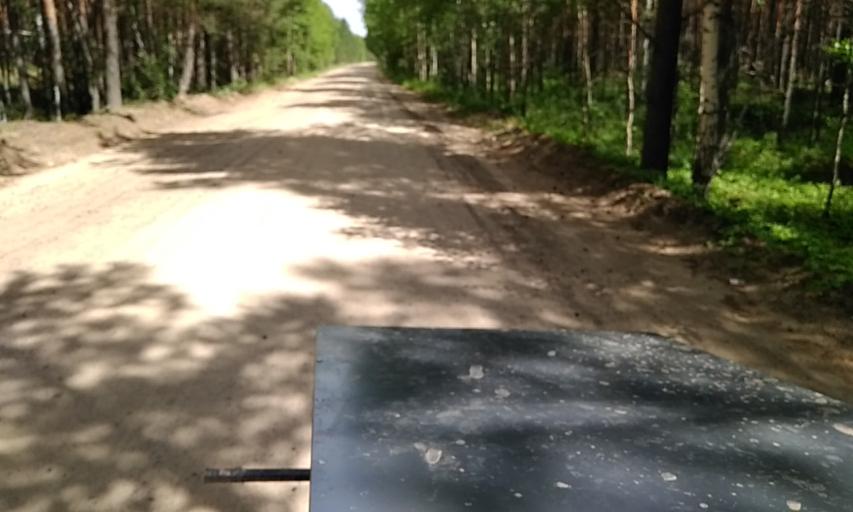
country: RU
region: Tomsk
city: Timiryazevskoye
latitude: 56.4204
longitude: 84.6798
